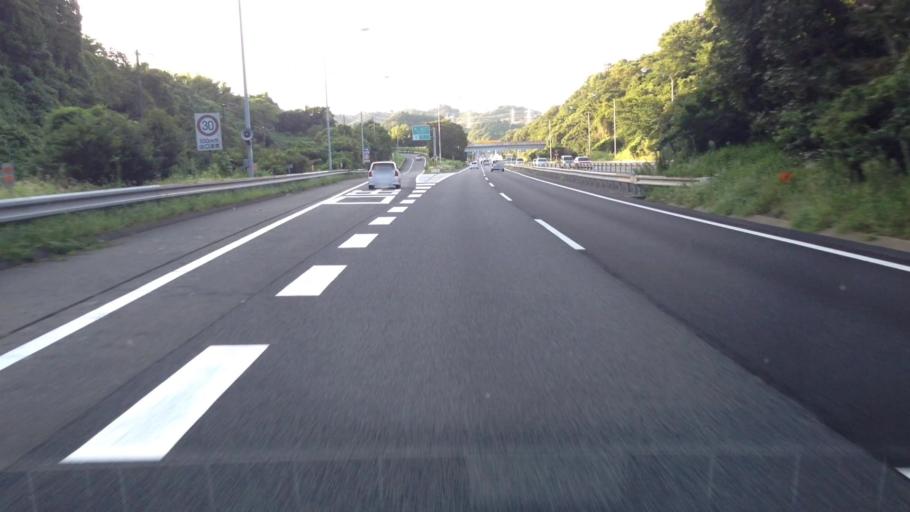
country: JP
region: Kanagawa
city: Zushi
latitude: 35.2885
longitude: 139.6206
